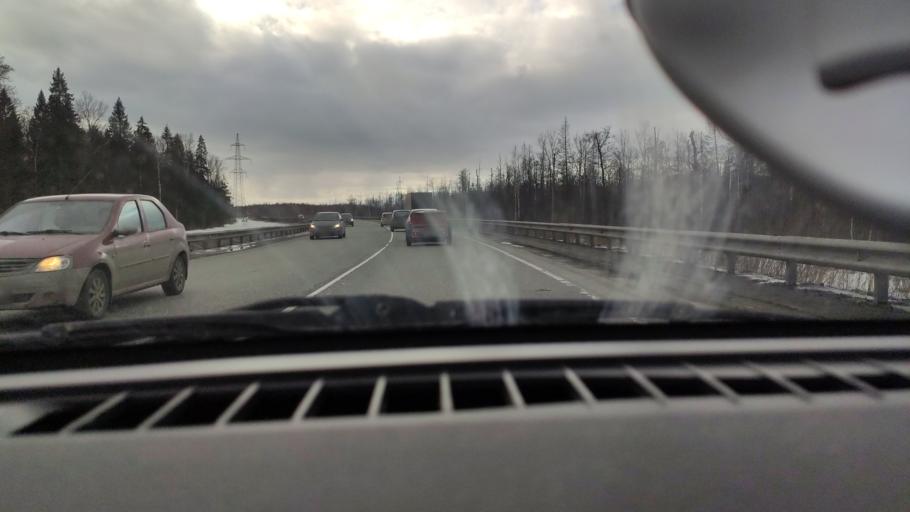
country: RU
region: Perm
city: Krasnokamsk
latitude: 58.1093
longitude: 55.7984
